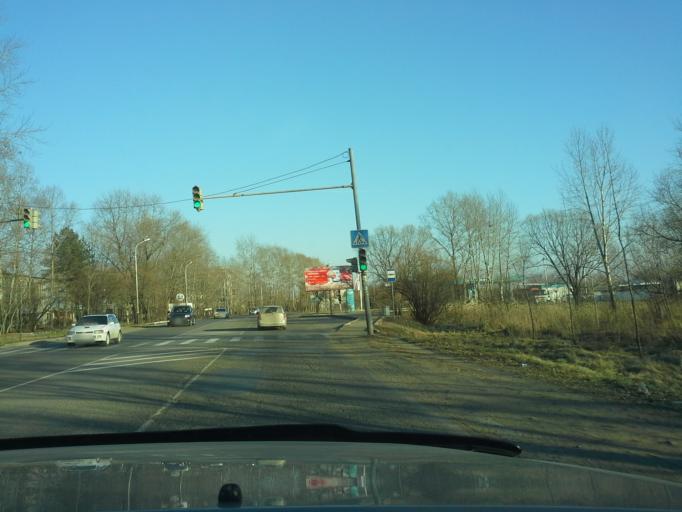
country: RU
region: Khabarovsk Krai
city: Topolevo
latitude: 48.4801
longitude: 135.1465
